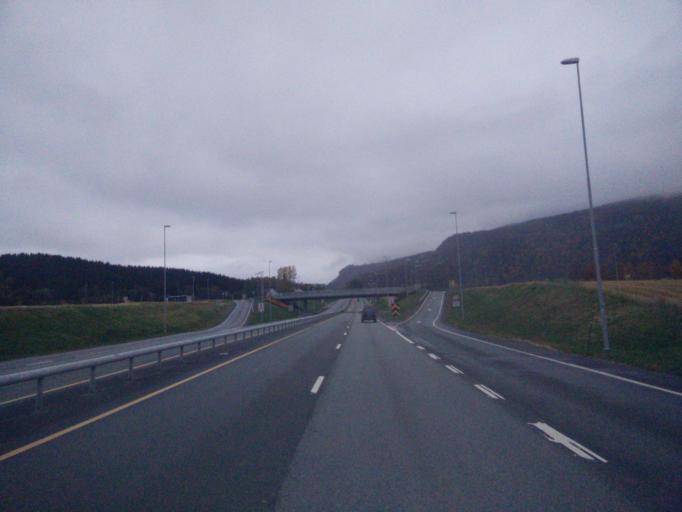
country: NO
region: Nord-Trondelag
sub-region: Stjordal
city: Stjordal
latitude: 63.4884
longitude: 10.8857
